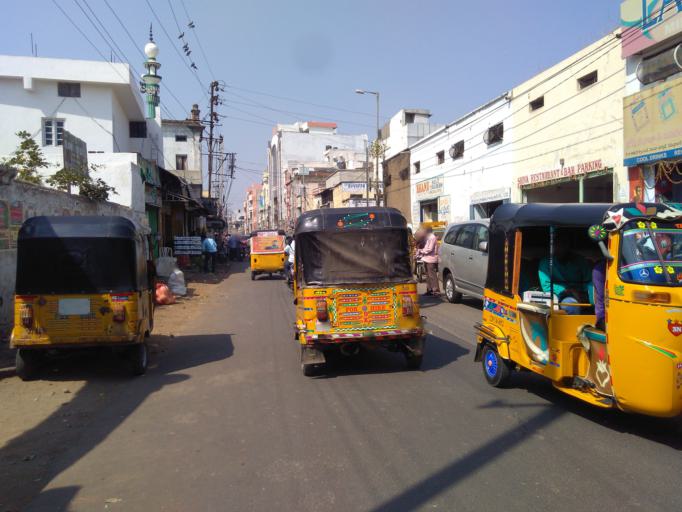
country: IN
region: Telangana
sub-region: Hyderabad
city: Malkajgiri
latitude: 17.4336
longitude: 78.4965
